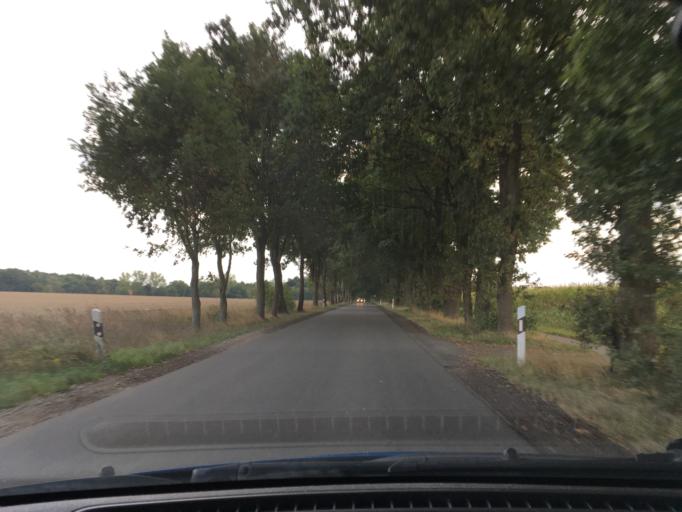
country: DE
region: Lower Saxony
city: Reppenstedt
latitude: 53.2417
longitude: 10.3668
